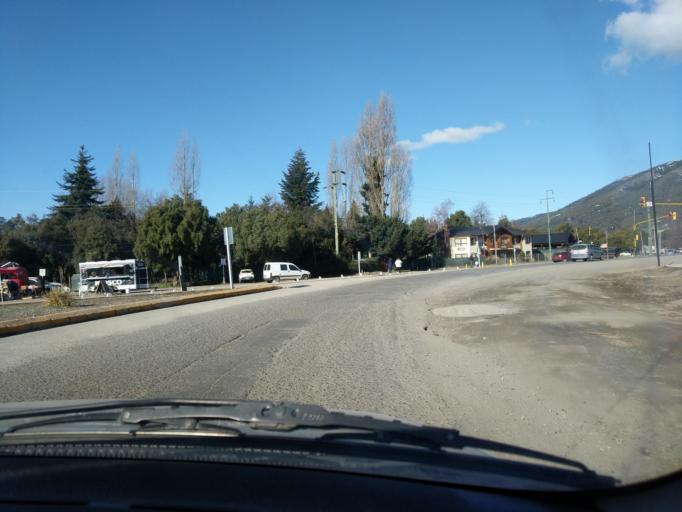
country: AR
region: Rio Negro
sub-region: Departamento de Bariloche
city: San Carlos de Bariloche
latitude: -41.1211
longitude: -71.4050
